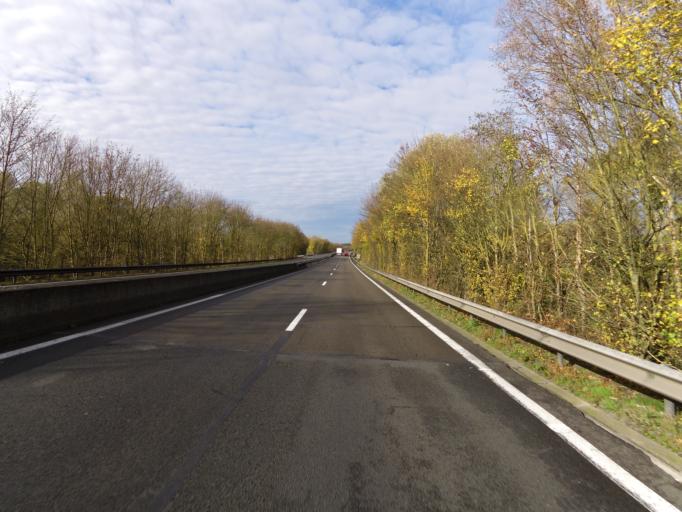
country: FR
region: Picardie
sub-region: Departement de l'Aisne
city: Itancourt
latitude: 49.7548
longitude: 3.3770
